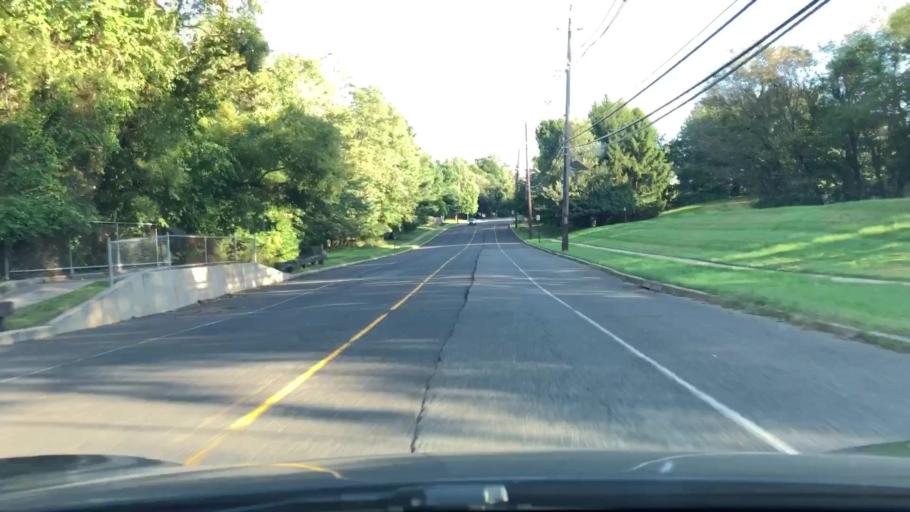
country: US
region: New Jersey
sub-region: Mercer County
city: Lawrenceville
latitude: 40.3082
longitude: -74.7324
